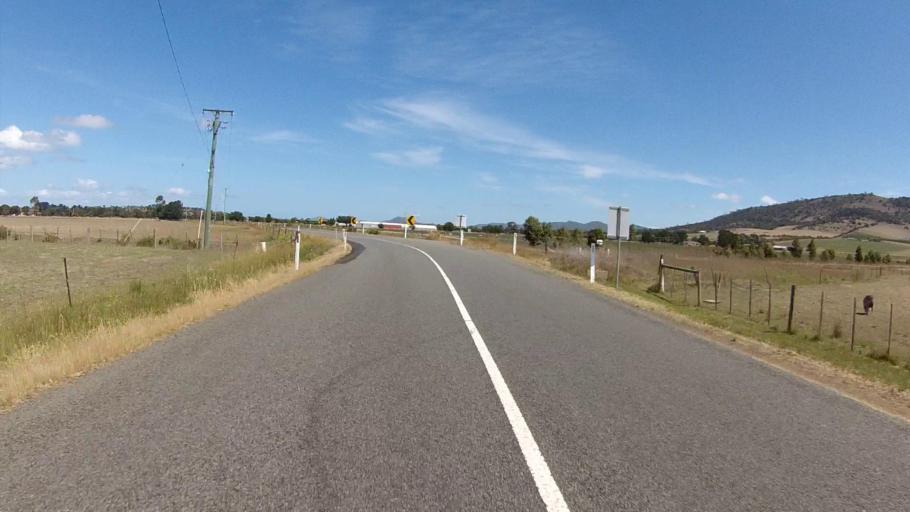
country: AU
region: Tasmania
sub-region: Sorell
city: Sorell
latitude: -42.7673
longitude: 147.5170
